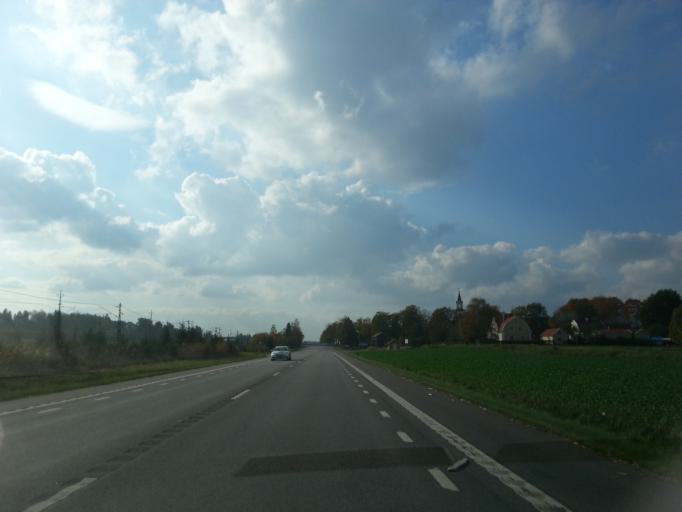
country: SE
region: OEstergoetland
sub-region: Linkopings Kommun
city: Linghem
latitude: 58.4521
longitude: 15.8371
